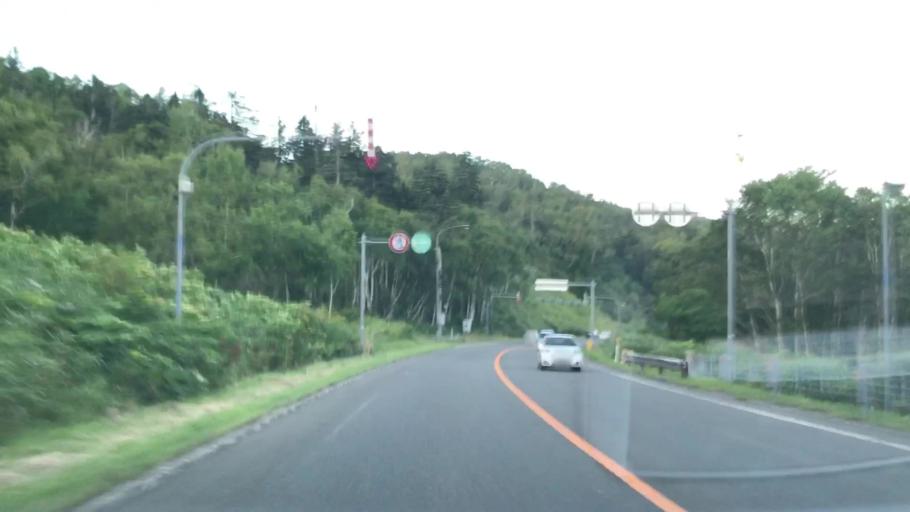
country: JP
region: Hokkaido
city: Sapporo
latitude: 42.8709
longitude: 141.1136
